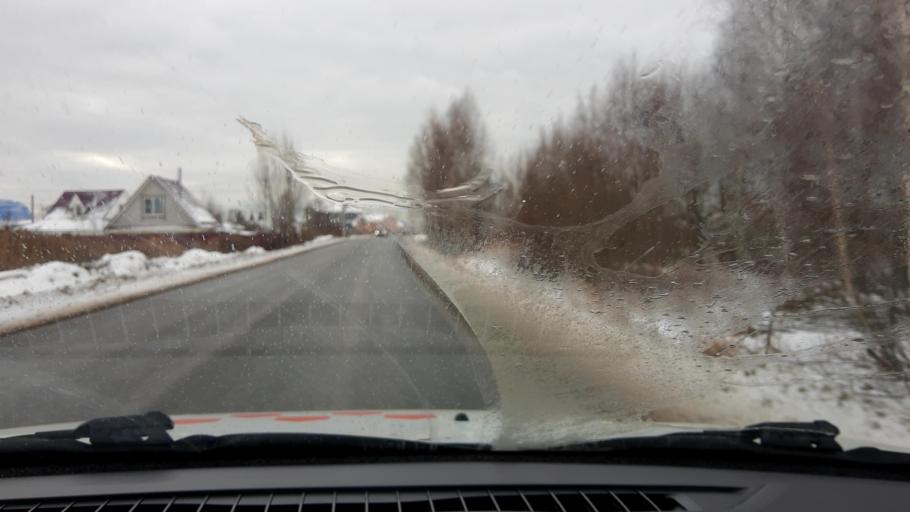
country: RU
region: Nizjnij Novgorod
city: Neklyudovo
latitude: 56.4261
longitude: 43.9636
